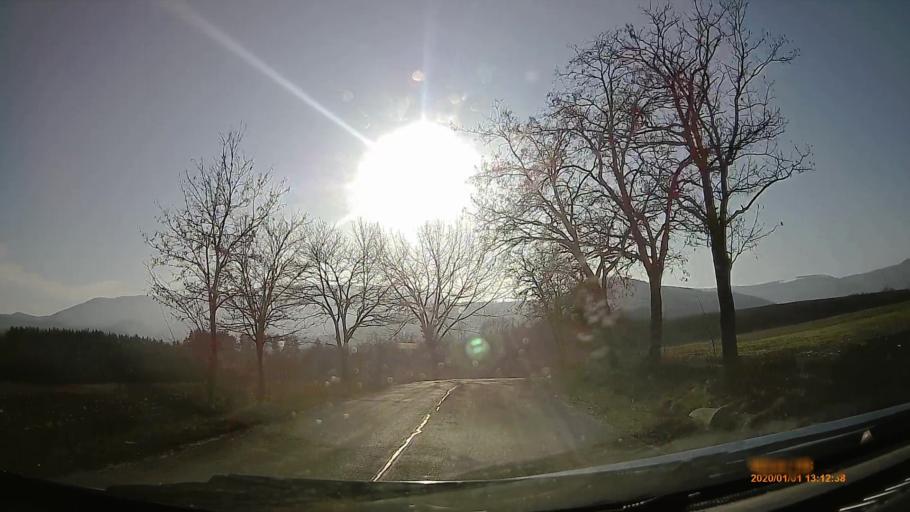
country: HU
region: Heves
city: Parad
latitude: 47.9305
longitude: 20.0247
